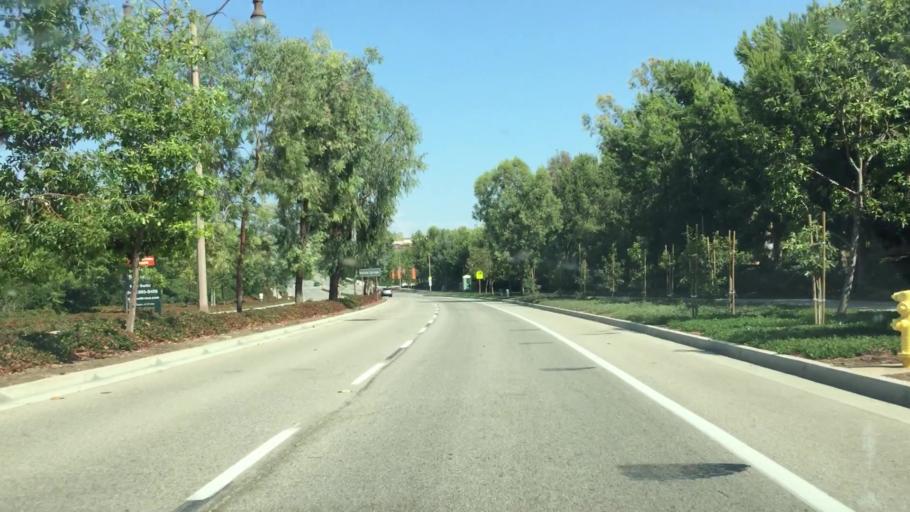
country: US
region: California
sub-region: Orange County
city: Foothill Ranch
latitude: 33.6971
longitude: -117.7152
